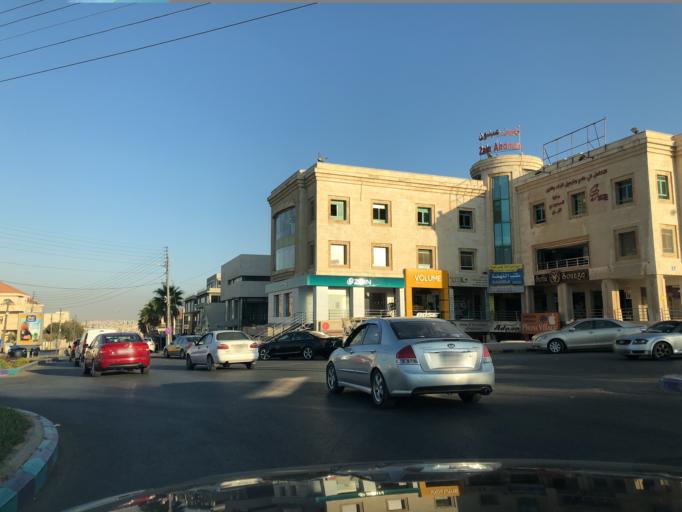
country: JO
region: Amman
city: Al Bunayyat ash Shamaliyah
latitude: 31.9424
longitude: 35.8803
